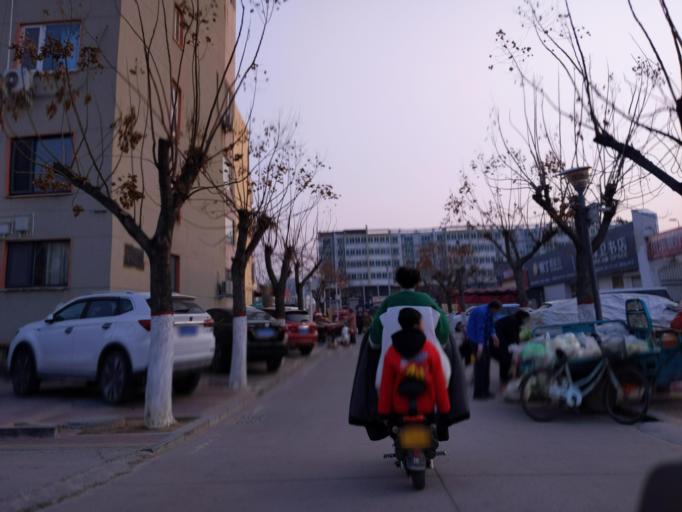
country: CN
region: Henan Sheng
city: Zhongyuanlu
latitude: 35.7711
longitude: 115.0885
